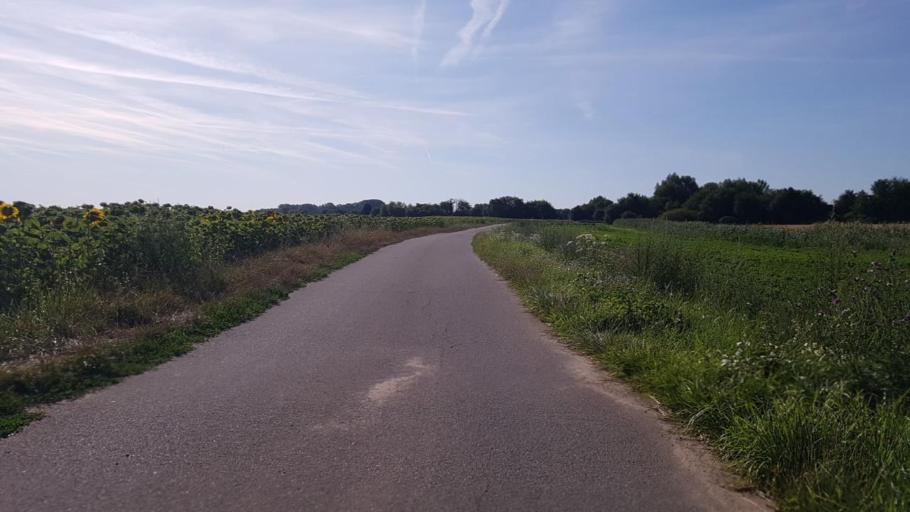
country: DE
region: Baden-Wuerttemberg
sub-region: Karlsruhe Region
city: Sankt Leon-Rot
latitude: 49.2866
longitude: 8.5950
